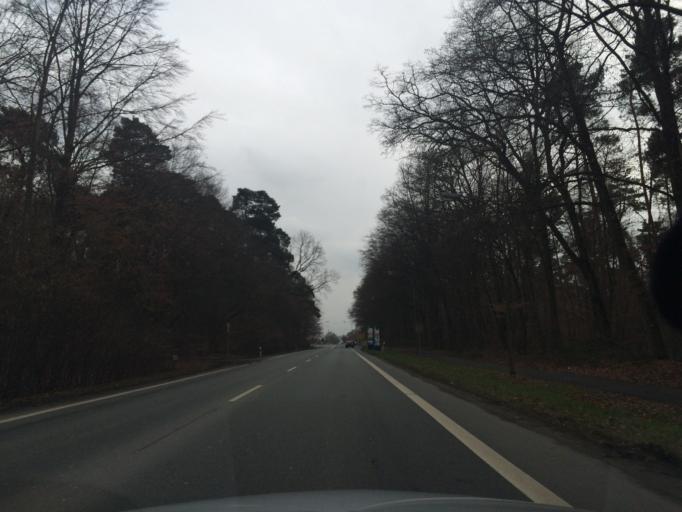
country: DE
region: Hesse
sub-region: Regierungsbezirk Darmstadt
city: Neu Isenburg
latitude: 50.0387
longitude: 8.6953
